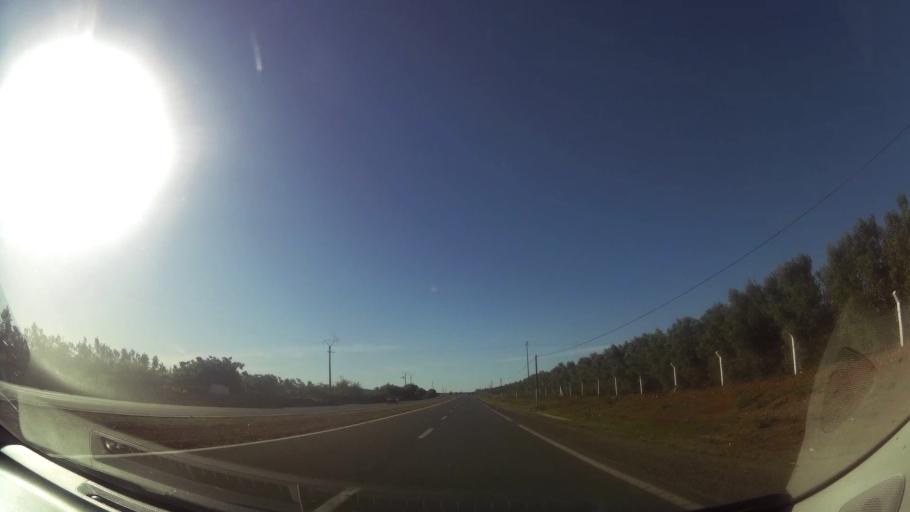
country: MA
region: Oriental
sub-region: Berkane-Taourirt
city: Ahfir
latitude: 35.0142
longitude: -2.1990
